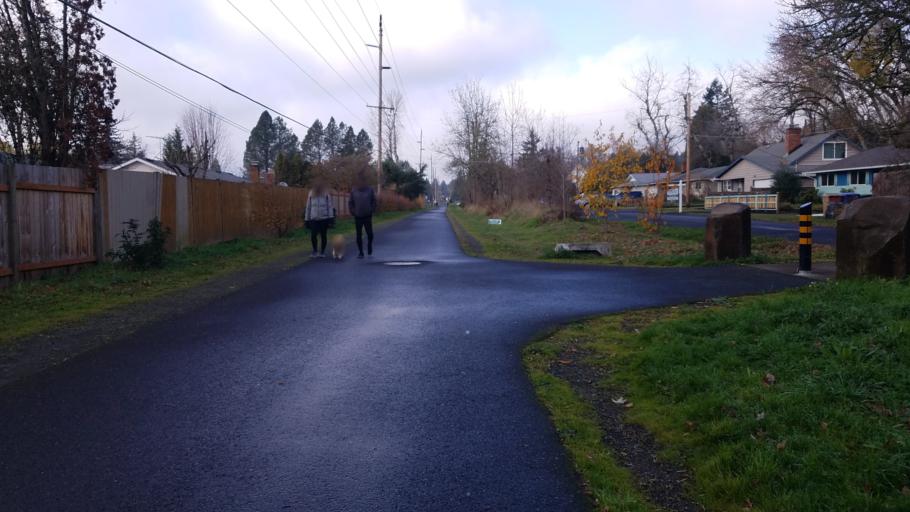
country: US
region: Oregon
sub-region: Clackamas County
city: Oak Grove
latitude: 45.4047
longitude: -122.6323
